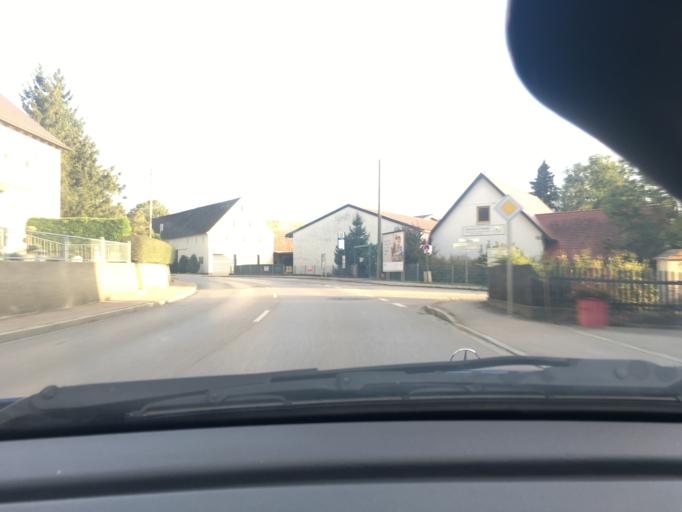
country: DE
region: Bavaria
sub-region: Swabia
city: Gablingen
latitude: 48.4134
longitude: 10.8246
